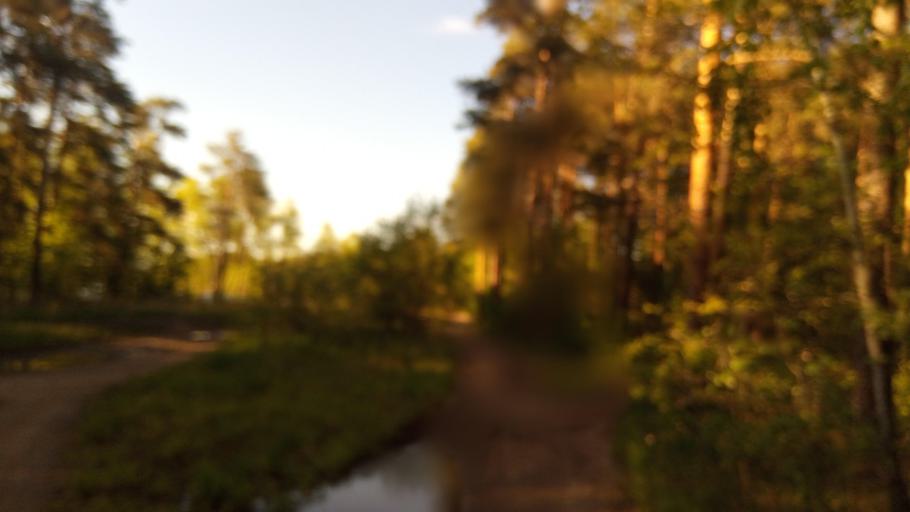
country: RU
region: Chelyabinsk
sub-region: Gorod Chelyabinsk
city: Chelyabinsk
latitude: 55.1379
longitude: 61.3290
